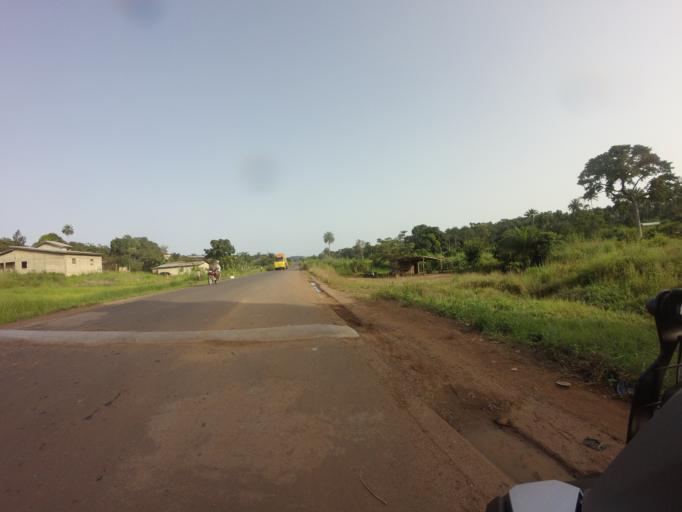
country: GN
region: Nzerekore
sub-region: Nzerekore Prefecture
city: Nzerekore
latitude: 8.0342
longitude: -9.0203
